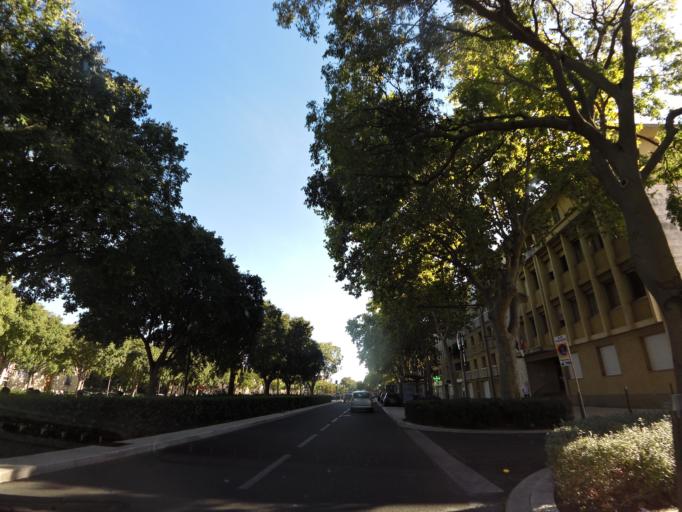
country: FR
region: Languedoc-Roussillon
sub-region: Departement du Gard
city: Nimes
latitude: 43.8373
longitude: 4.3501
